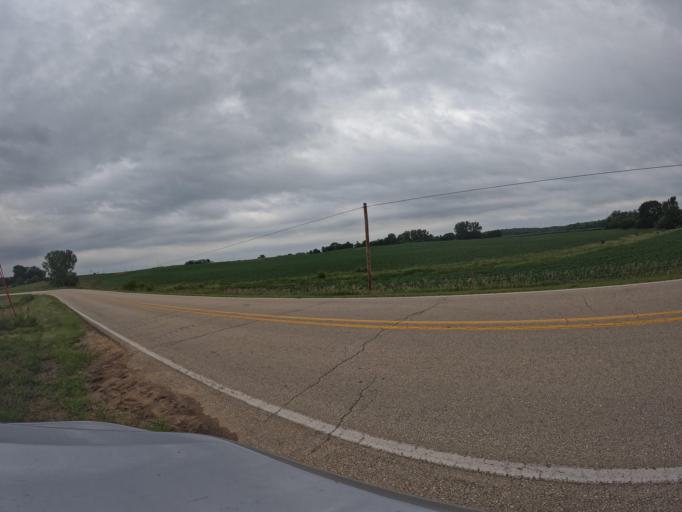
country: US
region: Iowa
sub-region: Clinton County
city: De Witt
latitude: 41.8693
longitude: -90.5767
